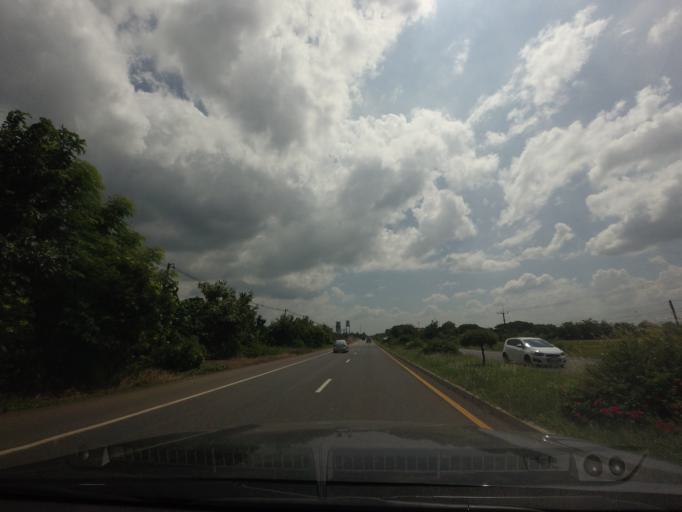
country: TH
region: Phetchabun
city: Nong Phai
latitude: 16.2075
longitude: 101.0890
